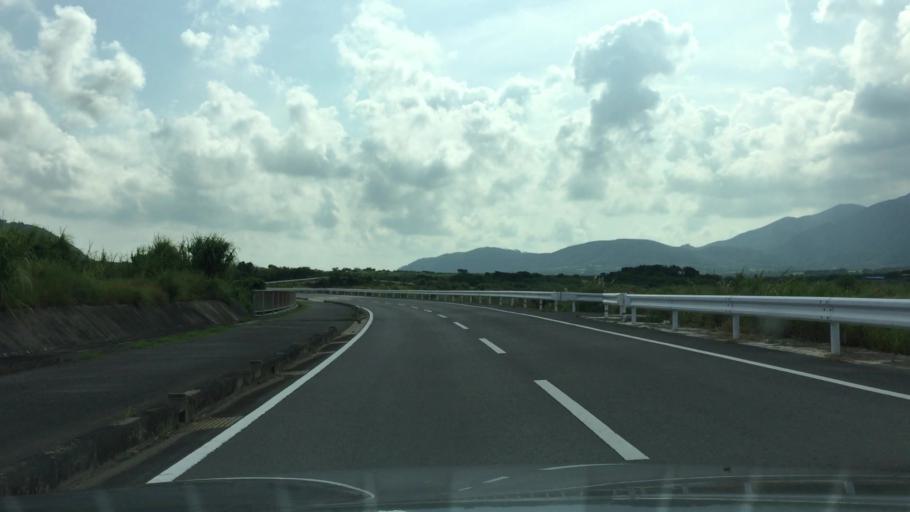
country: JP
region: Okinawa
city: Ishigaki
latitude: 24.4154
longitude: 124.2328
